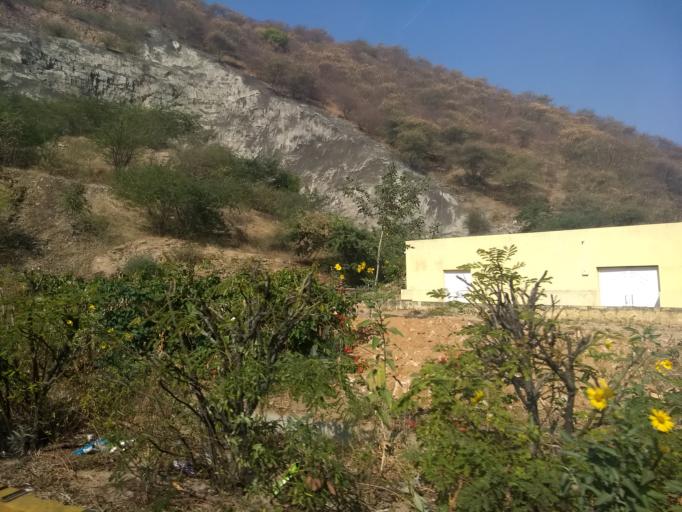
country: IN
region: Rajasthan
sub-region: Jaipur
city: Jaipur
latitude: 26.8929
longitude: 75.8578
